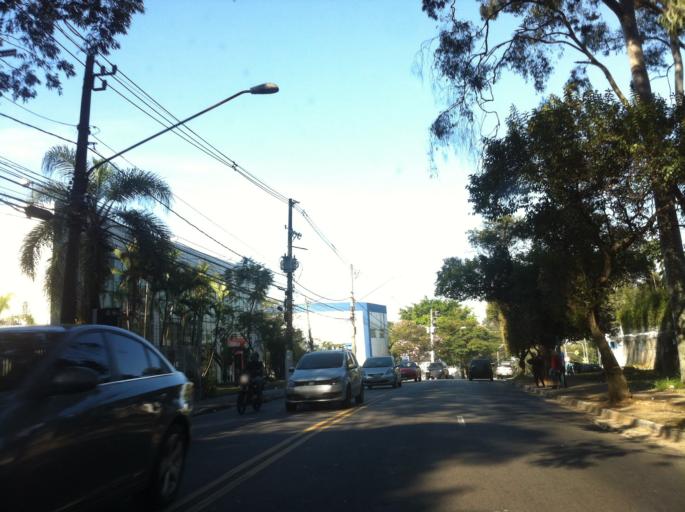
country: BR
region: Sao Paulo
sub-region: Diadema
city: Diadema
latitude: -23.6520
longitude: -46.6820
